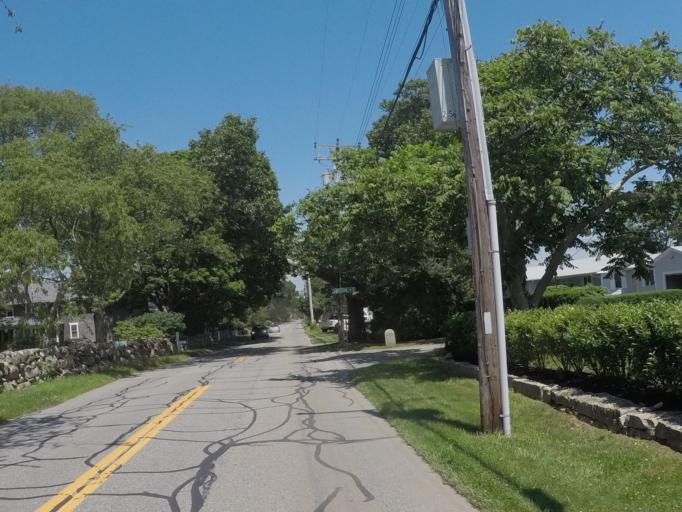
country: US
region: Massachusetts
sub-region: Bristol County
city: Bliss Corner
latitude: 41.5456
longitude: -70.9546
